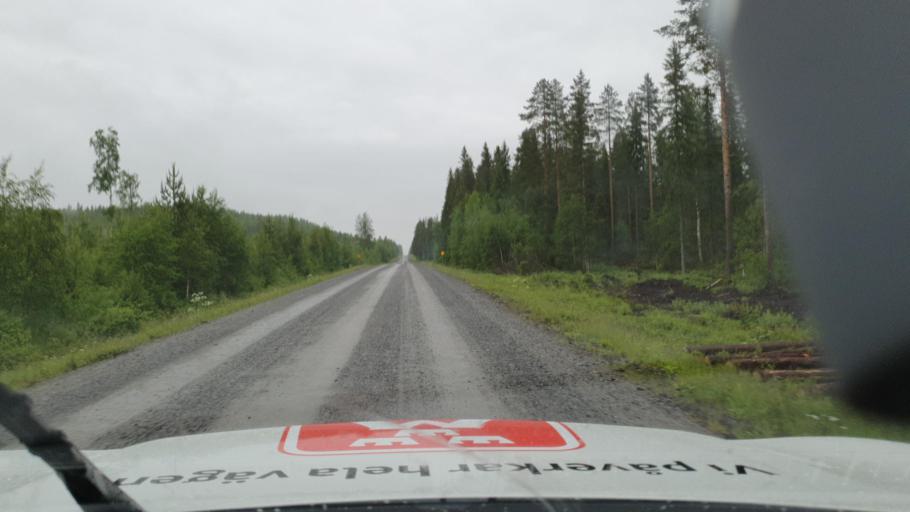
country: SE
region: Vaesterbotten
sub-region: Bjurholms Kommun
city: Bjurholm
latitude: 63.8511
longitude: 19.4751
